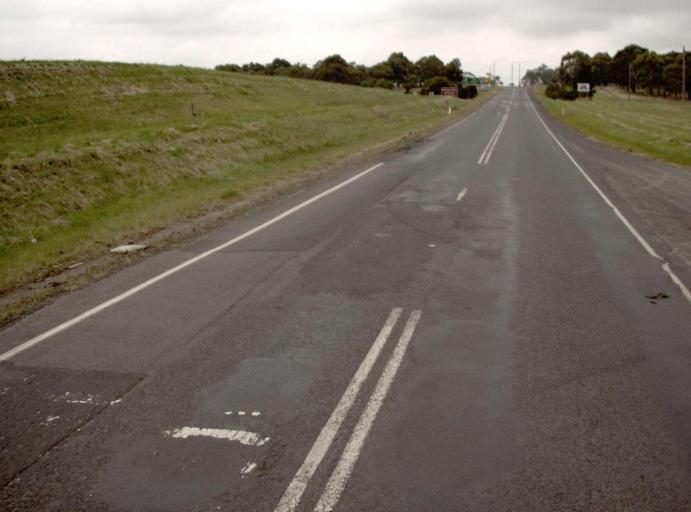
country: AU
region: Victoria
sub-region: Latrobe
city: Traralgon
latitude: -38.2498
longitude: 146.5435
